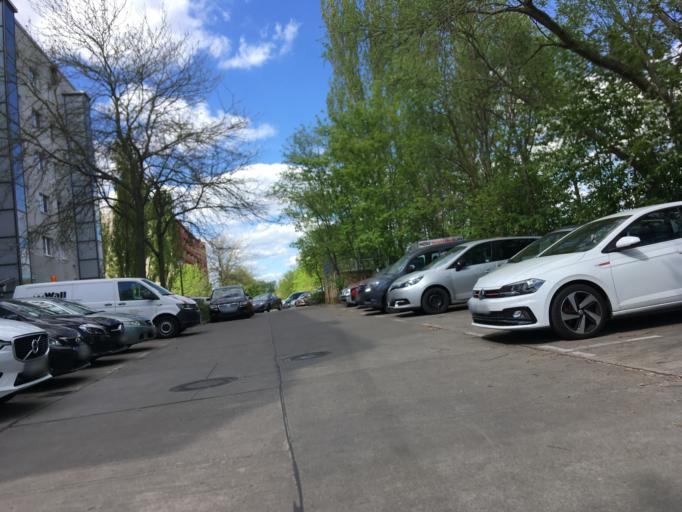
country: DE
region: Berlin
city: Hellersdorf
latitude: 52.5343
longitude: 13.6154
